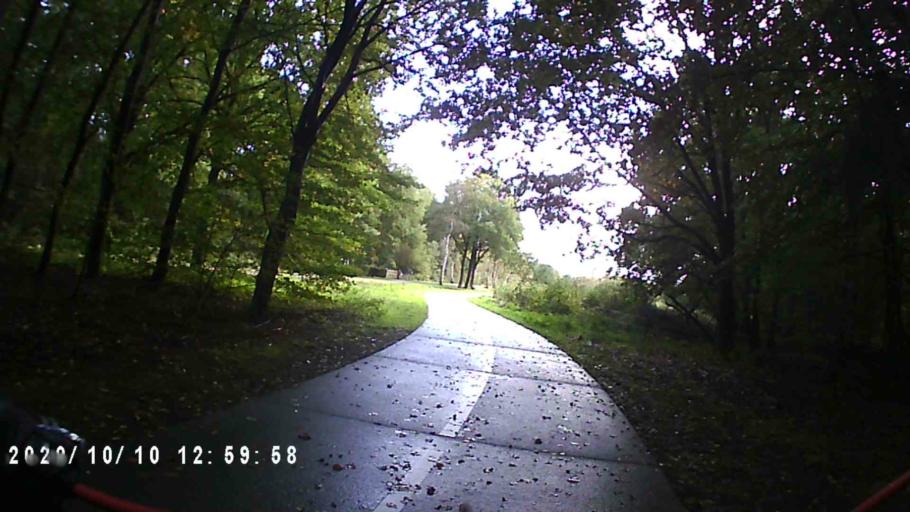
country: NL
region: Drenthe
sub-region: Gemeente Westerveld
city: Dwingeloo
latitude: 52.8981
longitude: 6.3010
